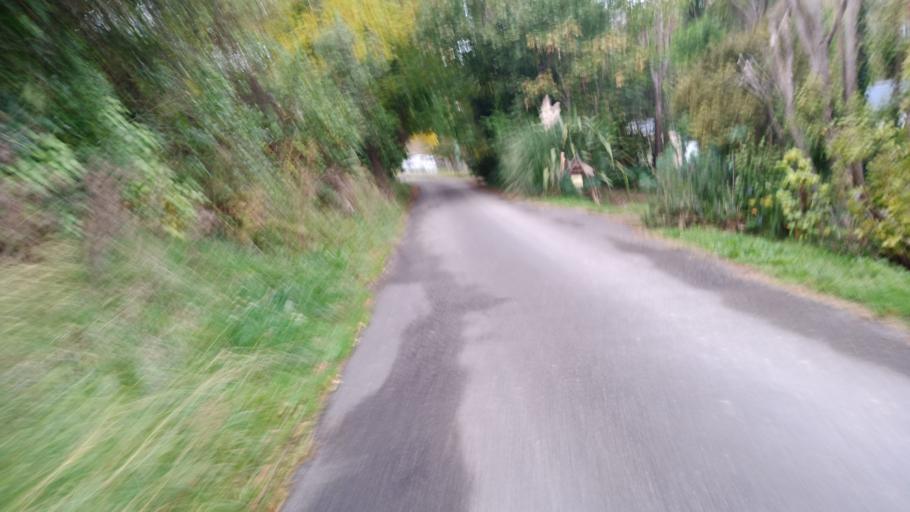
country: NZ
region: Gisborne
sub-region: Gisborne District
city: Gisborne
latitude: -38.6495
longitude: 178.0373
